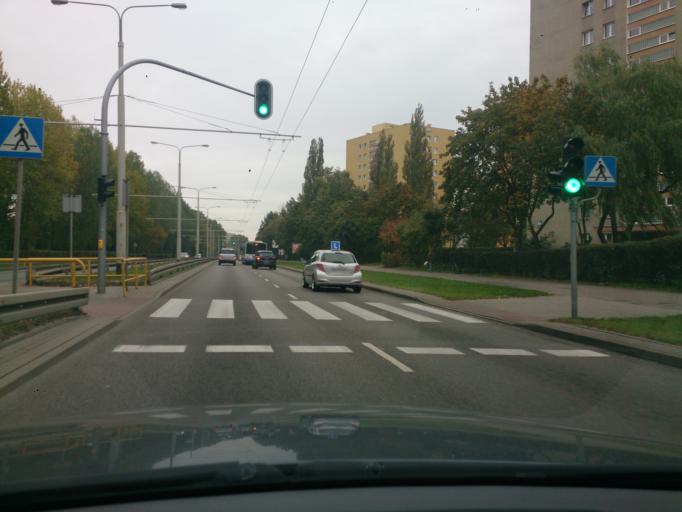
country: PL
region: Pomeranian Voivodeship
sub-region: Gdynia
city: Pogorze
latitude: 54.5407
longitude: 18.4644
